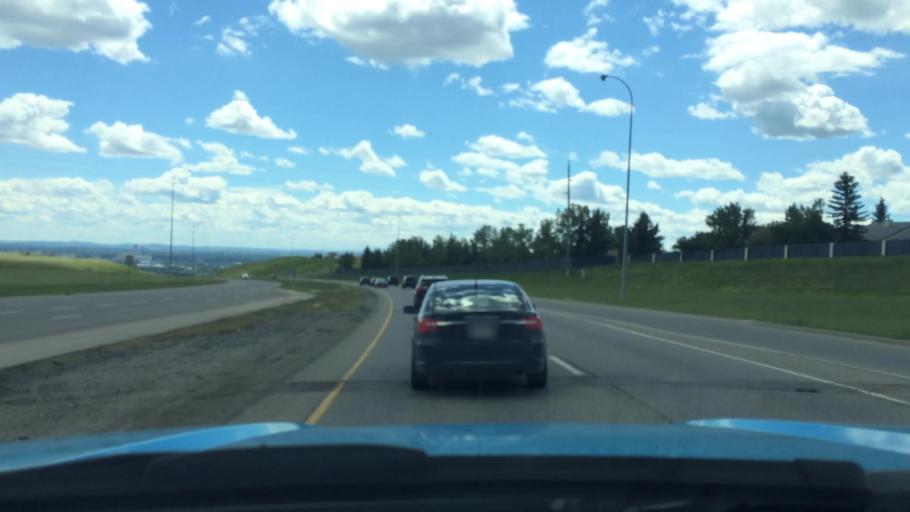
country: CA
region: Alberta
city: Calgary
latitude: 51.1261
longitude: -114.1338
